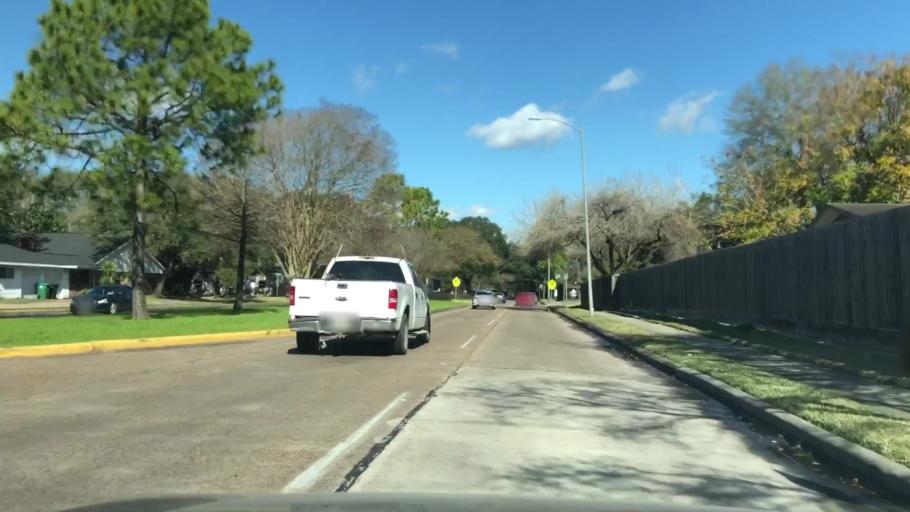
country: US
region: Texas
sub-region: Harris County
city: Bellaire
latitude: 29.6694
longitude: -95.4922
